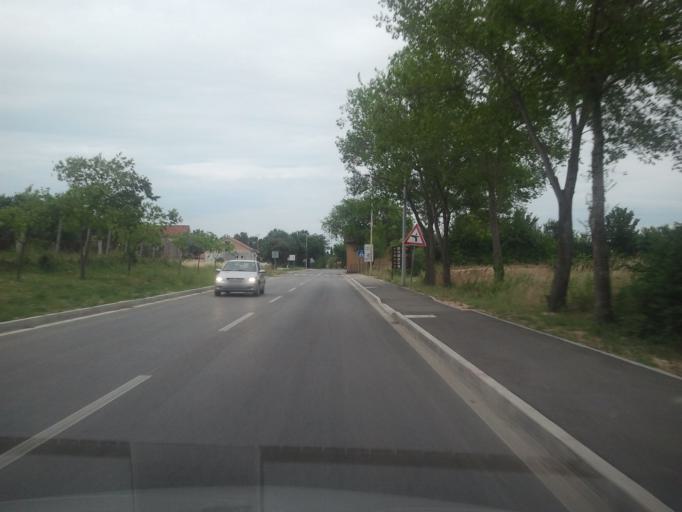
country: HR
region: Zadarska
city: Benkovac
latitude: 44.0293
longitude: 15.6103
